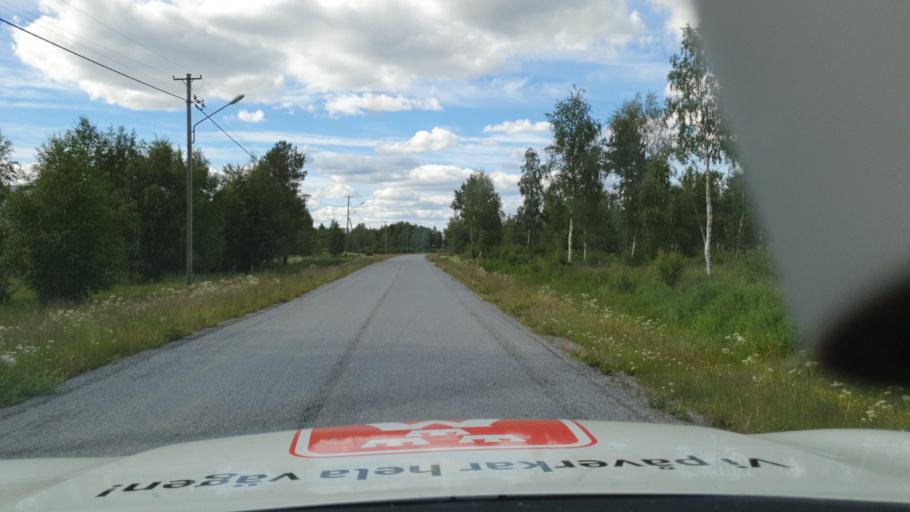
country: SE
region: Vaesterbotten
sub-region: Asele Kommun
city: Insjon
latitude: 64.1961
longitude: 17.7928
